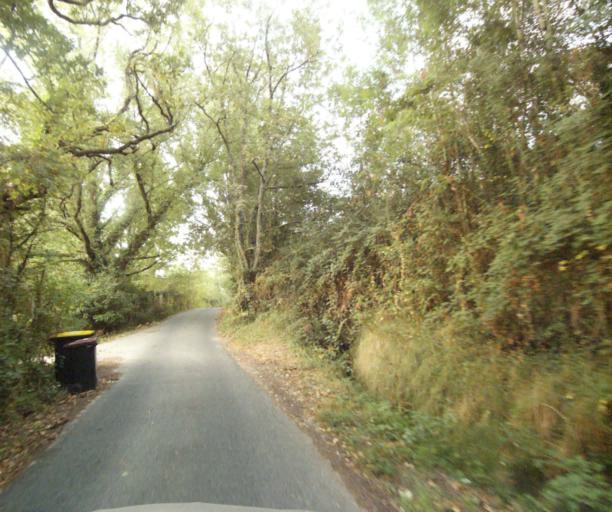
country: FR
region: Aquitaine
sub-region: Departement de la Gironde
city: Creon
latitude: 44.7741
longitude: -0.3365
